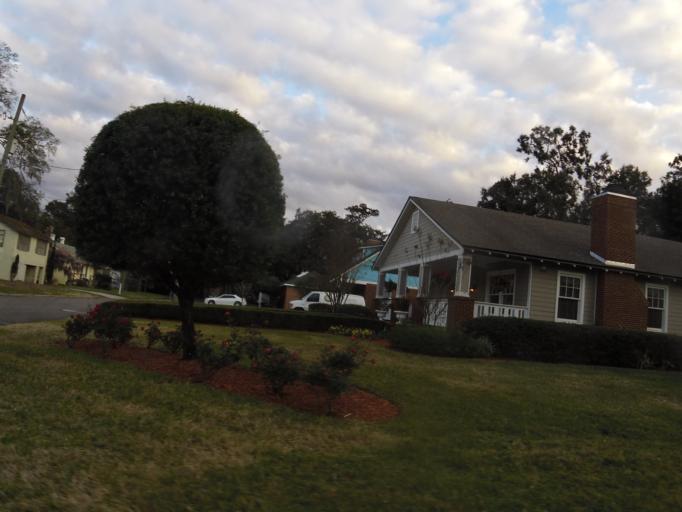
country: US
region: Florida
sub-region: Duval County
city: Jacksonville
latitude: 30.2938
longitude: -81.7144
